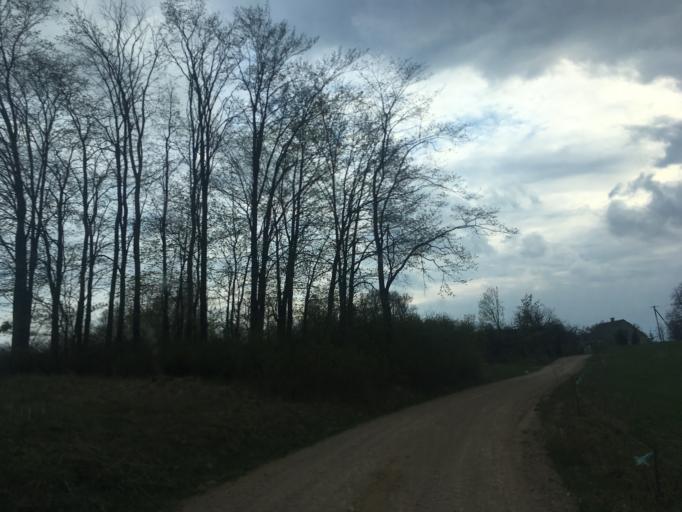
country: PL
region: Podlasie
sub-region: Powiat sejnenski
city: Punsk
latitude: 54.2867
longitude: 23.0989
